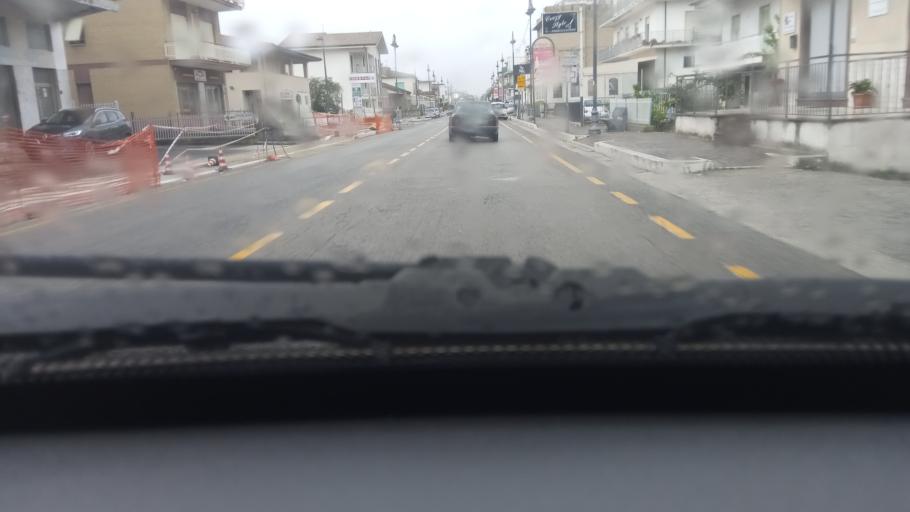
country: IT
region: Latium
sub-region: Provincia di Latina
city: Minturno
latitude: 41.2530
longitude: 13.7229
